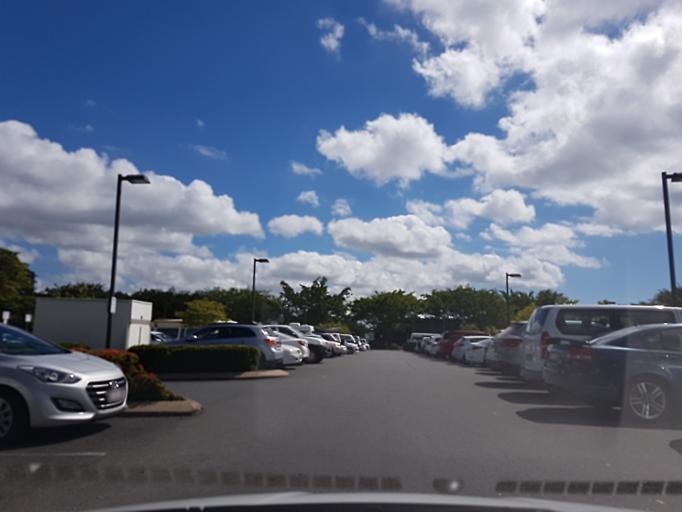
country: AU
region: Queensland
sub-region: Cairns
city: Cairns
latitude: -16.9206
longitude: 145.7795
